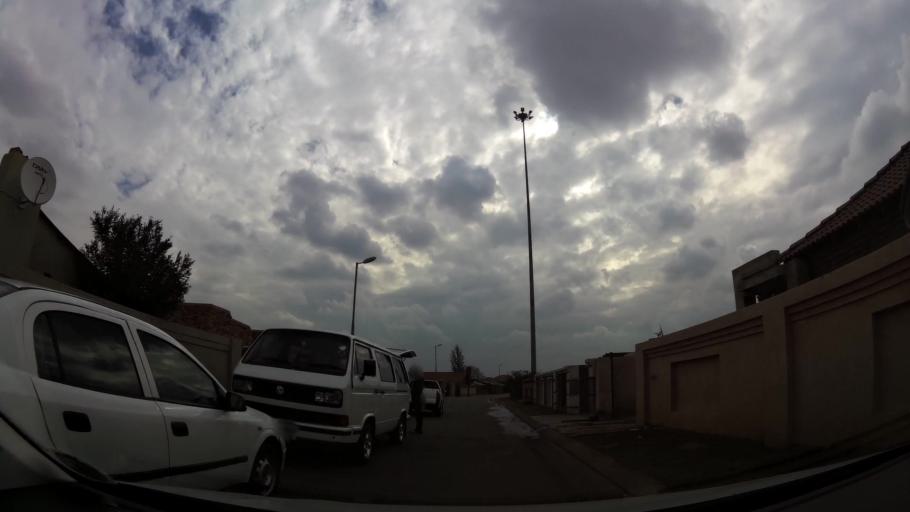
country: ZA
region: Gauteng
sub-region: City of Johannesburg Metropolitan Municipality
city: Soweto
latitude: -26.2673
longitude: 27.8511
